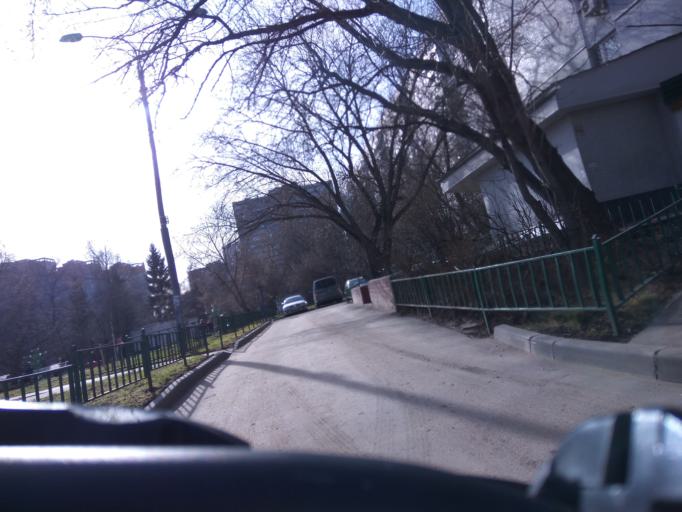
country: RU
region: Moscow
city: Davydkovo
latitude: 55.7267
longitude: 37.4740
